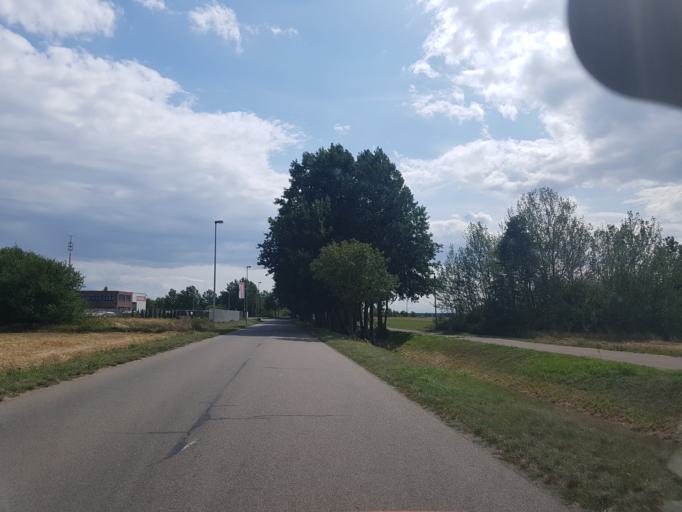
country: DE
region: Brandenburg
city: Herzberg
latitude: 51.6775
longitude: 13.2087
